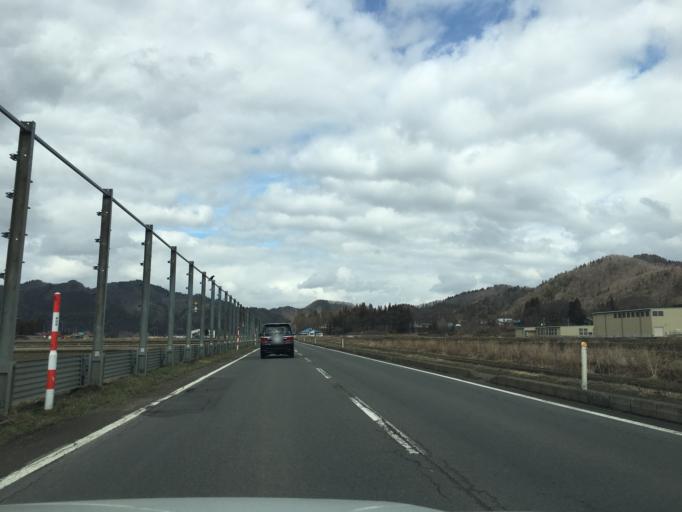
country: JP
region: Akita
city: Hanawa
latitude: 40.2313
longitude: 140.7328
